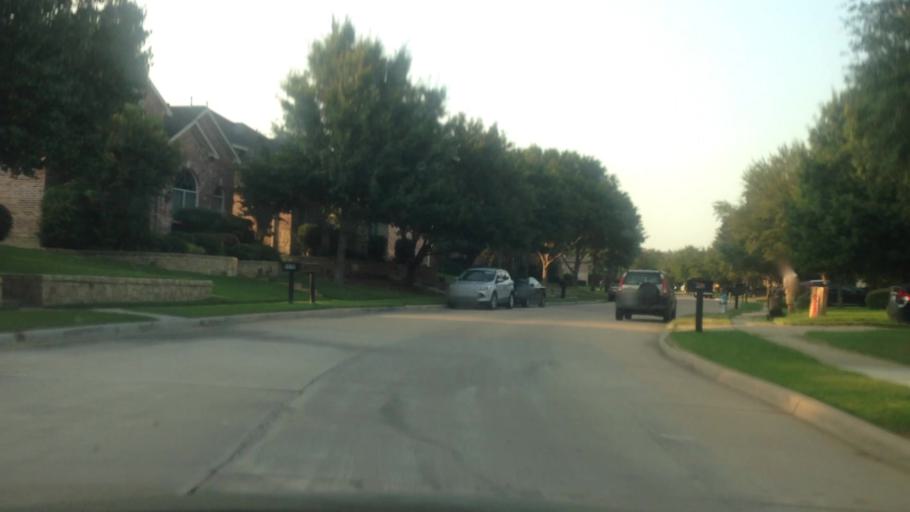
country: US
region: Texas
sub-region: Denton County
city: The Colony
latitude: 33.1246
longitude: -96.8683
